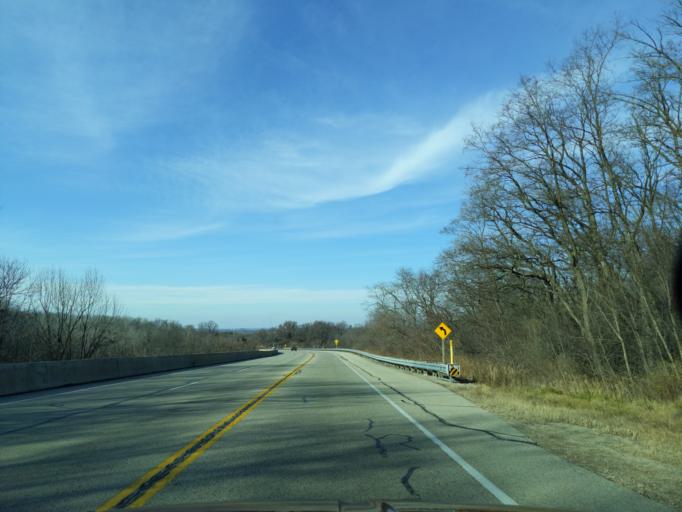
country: US
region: Wisconsin
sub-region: Walworth County
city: Whitewater
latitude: 42.8018
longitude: -88.6494
